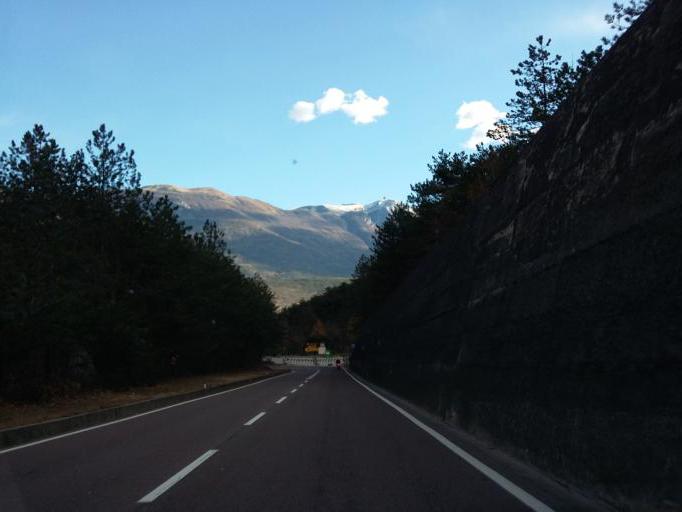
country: IT
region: Trentino-Alto Adige
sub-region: Provincia di Trento
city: Pietramurata
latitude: 46.0450
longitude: 10.9437
